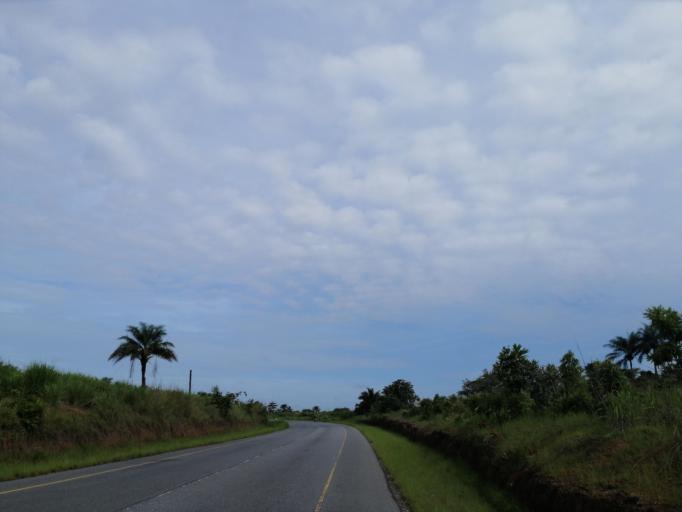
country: SL
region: Northern Province
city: Port Loko
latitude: 8.7725
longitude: -12.8627
